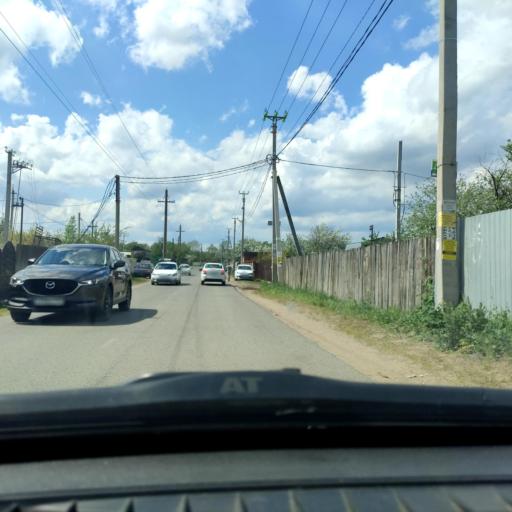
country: RU
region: Samara
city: Zhigulevsk
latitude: 53.4663
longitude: 49.6454
